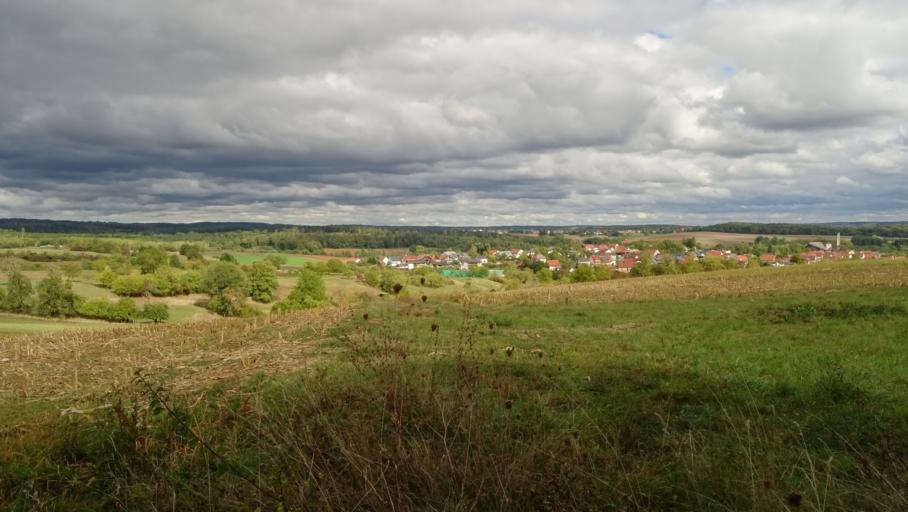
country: DE
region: Baden-Wuerttemberg
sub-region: Karlsruhe Region
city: Fahrenbach
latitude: 49.3994
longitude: 9.1247
